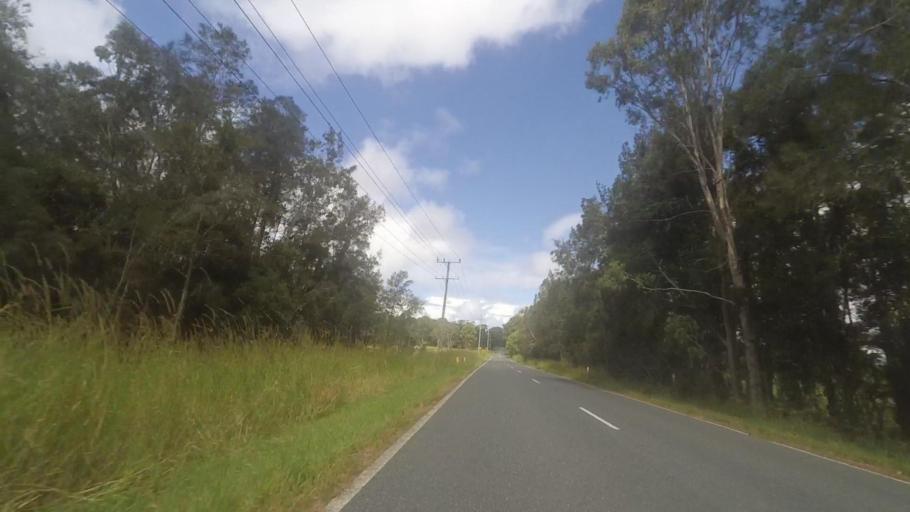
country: AU
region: New South Wales
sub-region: Great Lakes
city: Bulahdelah
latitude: -32.3876
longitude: 152.4142
